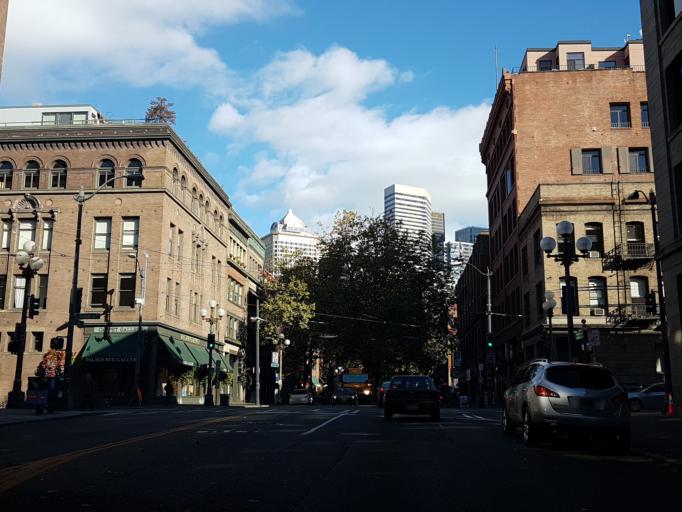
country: US
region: Washington
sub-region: King County
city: Seattle
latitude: 47.5987
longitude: -122.3343
